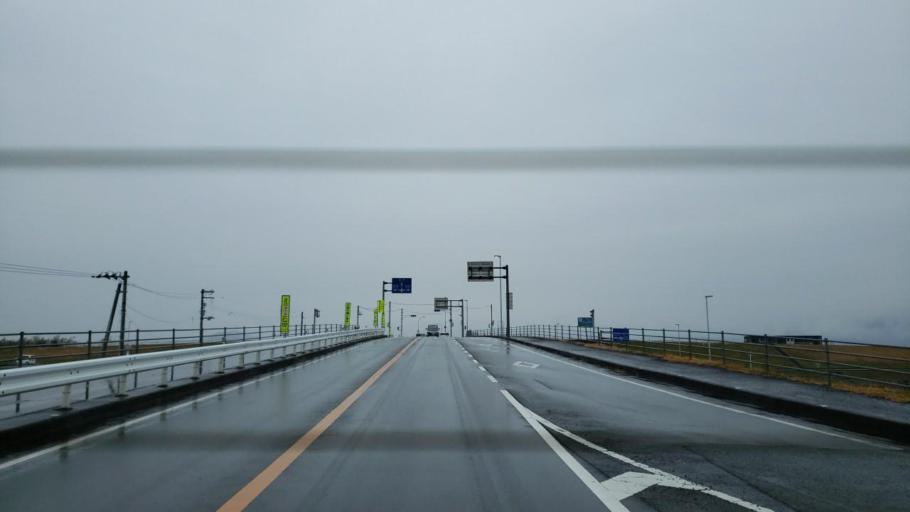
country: JP
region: Tokushima
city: Ishii
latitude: 34.1093
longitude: 134.4368
